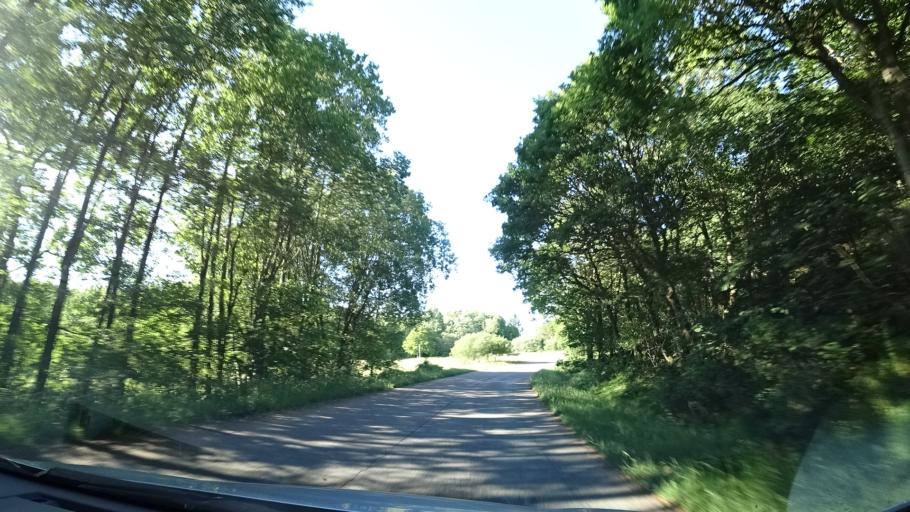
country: SE
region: Vaestra Goetaland
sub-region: Goteborg
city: Billdal
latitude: 57.5772
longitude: 11.9782
